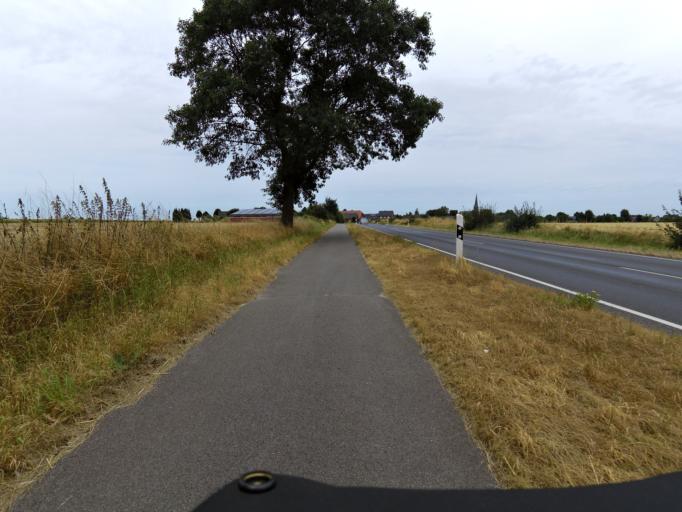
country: DE
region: North Rhine-Westphalia
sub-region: Regierungsbezirk Dusseldorf
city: Weeze
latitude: 51.5812
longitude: 6.1789
